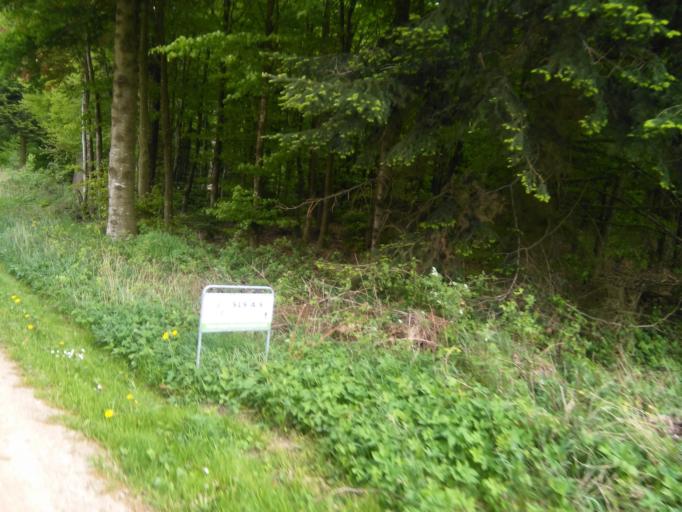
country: DK
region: Central Jutland
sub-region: Horsens Kommune
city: Braedstrup
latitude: 56.0477
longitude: 9.6136
